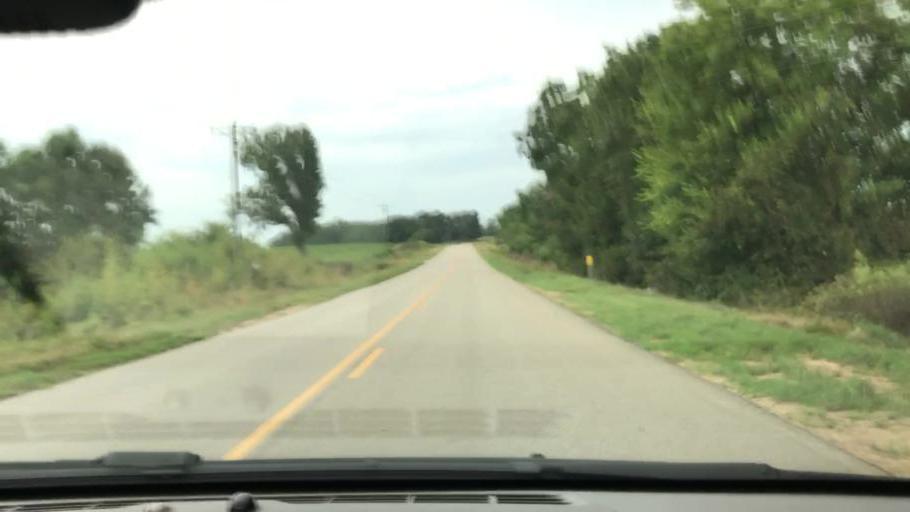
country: US
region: Alabama
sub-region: Houston County
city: Ashford
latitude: 31.2284
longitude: -85.1822
